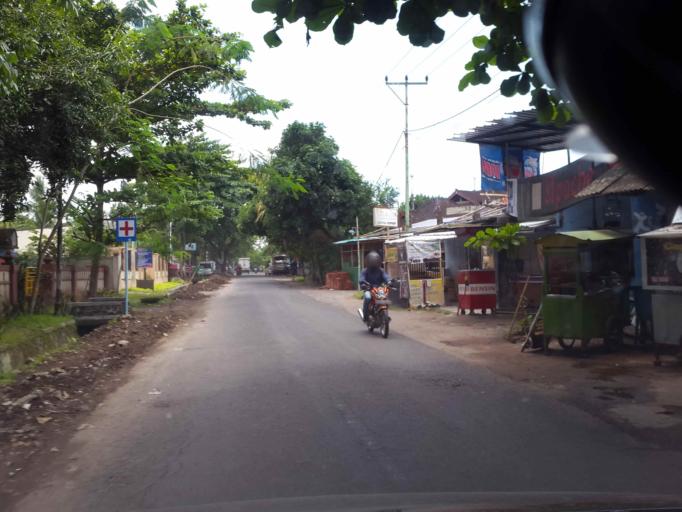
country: ID
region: West Nusa Tenggara
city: Mambalan
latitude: -8.5400
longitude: 116.0989
